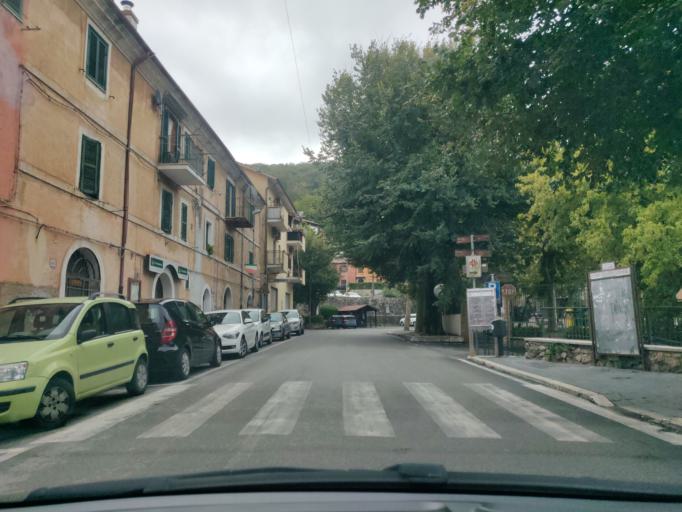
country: IT
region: Latium
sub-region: Citta metropolitana di Roma Capitale
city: Allumiere
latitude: 42.1543
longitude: 11.9053
